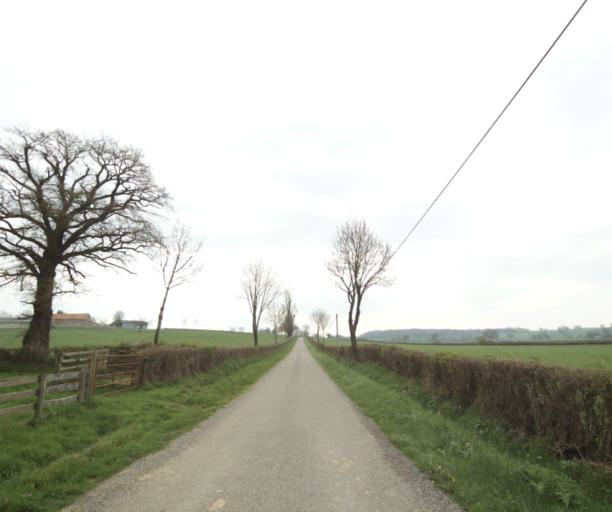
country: FR
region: Bourgogne
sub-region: Departement de Saone-et-Loire
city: Paray-le-Monial
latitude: 46.4789
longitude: 4.1756
